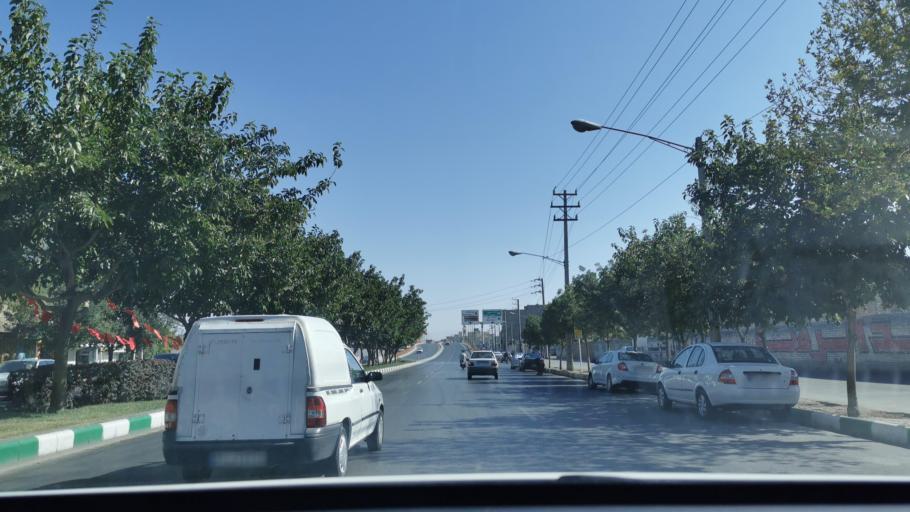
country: IR
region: Razavi Khorasan
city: Mashhad
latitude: 36.3338
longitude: 59.6029
